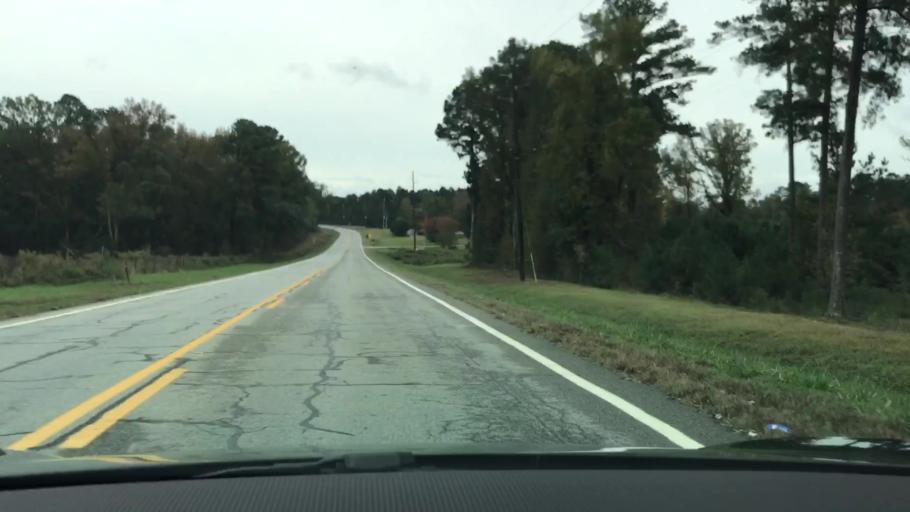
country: US
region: Georgia
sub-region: Warren County
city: Warrenton
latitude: 33.3963
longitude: -82.6522
